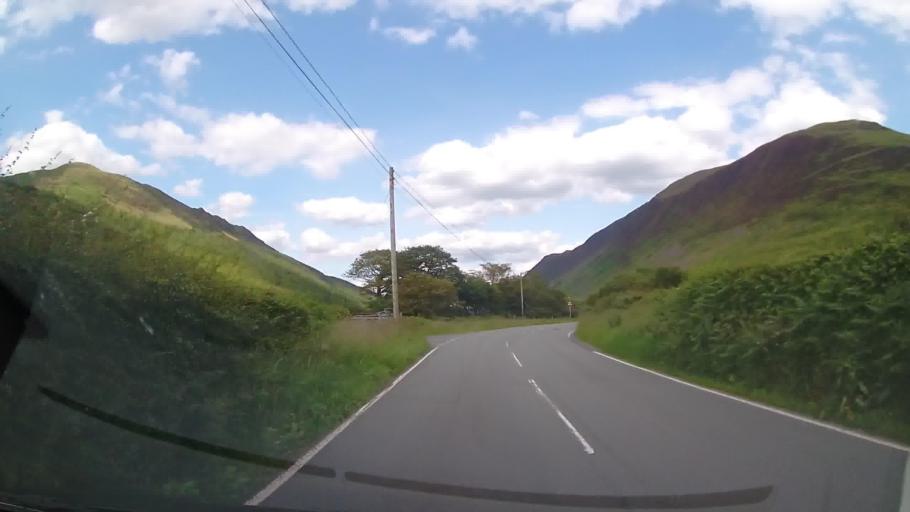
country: GB
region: Wales
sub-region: Gwynedd
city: Corris
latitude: 52.6516
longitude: -3.9393
